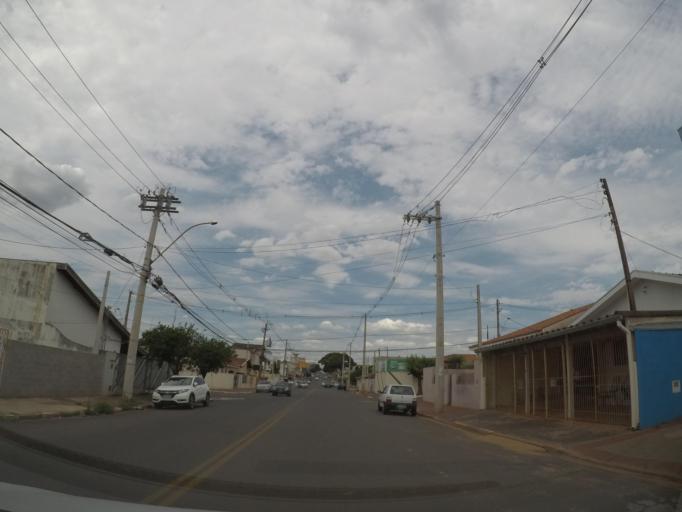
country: BR
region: Sao Paulo
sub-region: Sumare
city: Sumare
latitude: -22.8292
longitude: -47.2757
